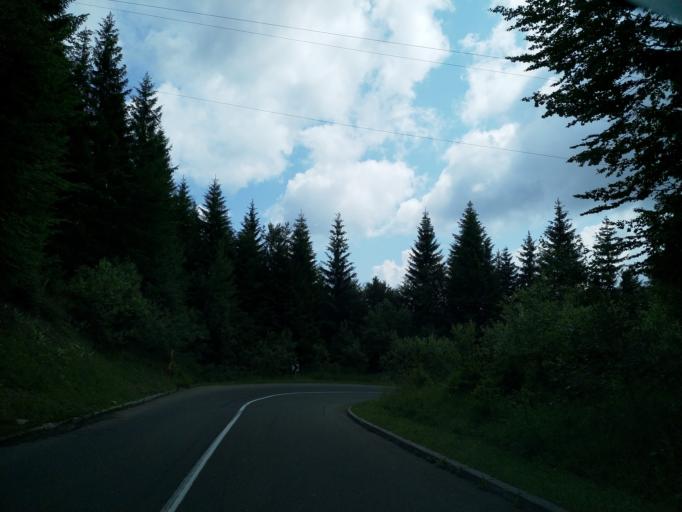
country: XK
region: Mitrovica
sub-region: Komuna e Leposaviqit
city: Leposaviq
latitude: 43.2745
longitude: 20.7883
